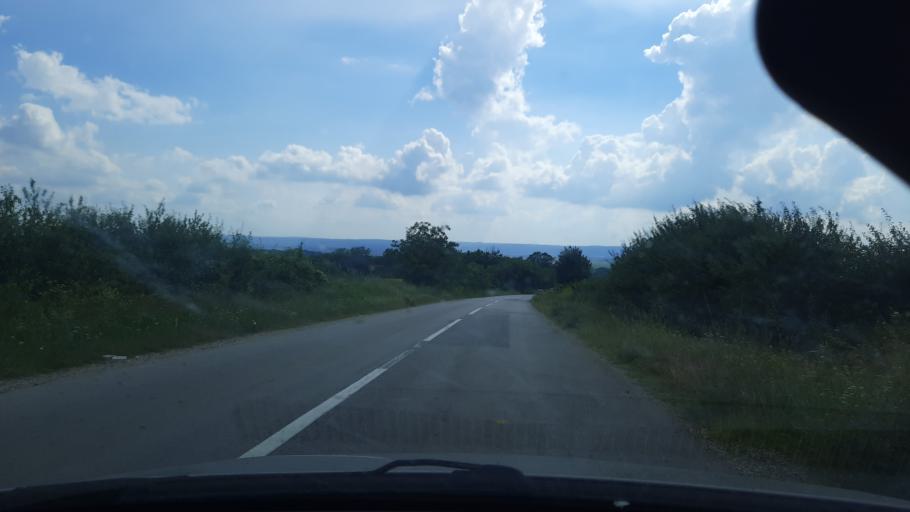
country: RS
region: Central Serbia
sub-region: Branicevski Okrug
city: Malo Crnice
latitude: 44.5769
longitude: 21.3822
